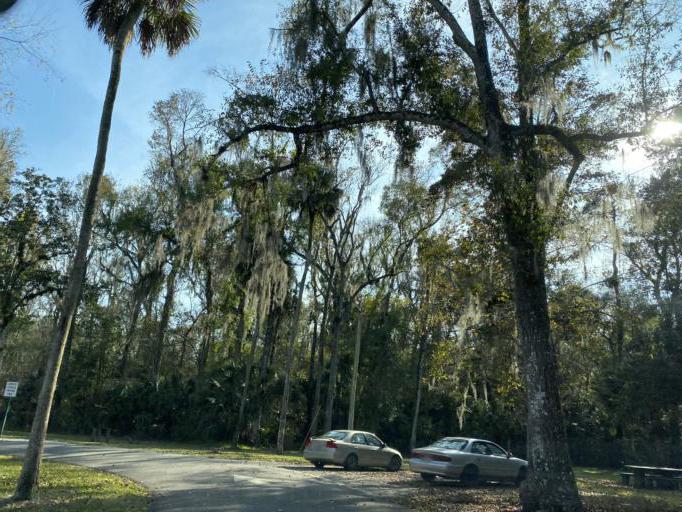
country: US
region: Florida
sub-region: Seminole County
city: Longwood
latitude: 28.7206
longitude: -81.3319
